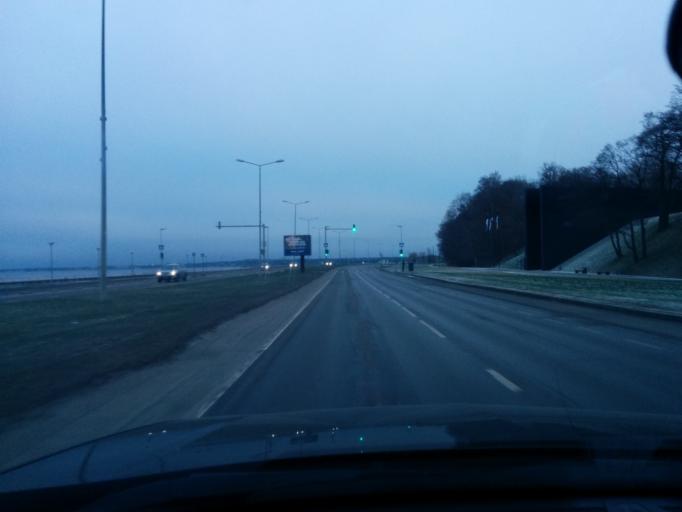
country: EE
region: Harju
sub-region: Viimsi vald
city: Viimsi
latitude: 59.4561
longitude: 24.8104
